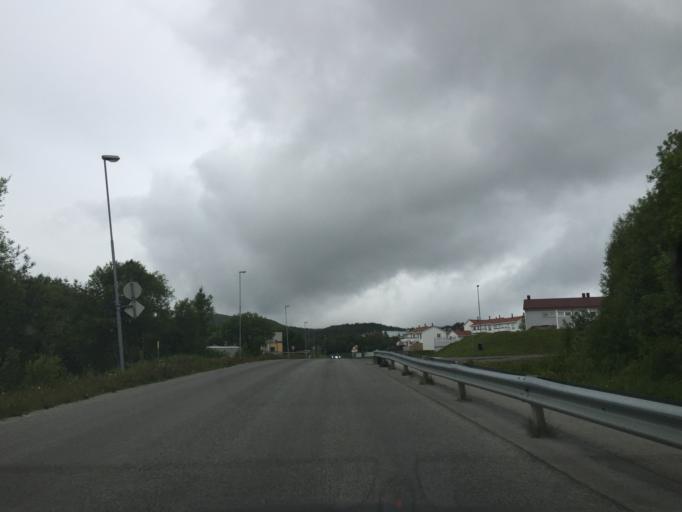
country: NO
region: Nordland
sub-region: Bodo
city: Lopsmarka
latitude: 67.2879
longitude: 14.5732
